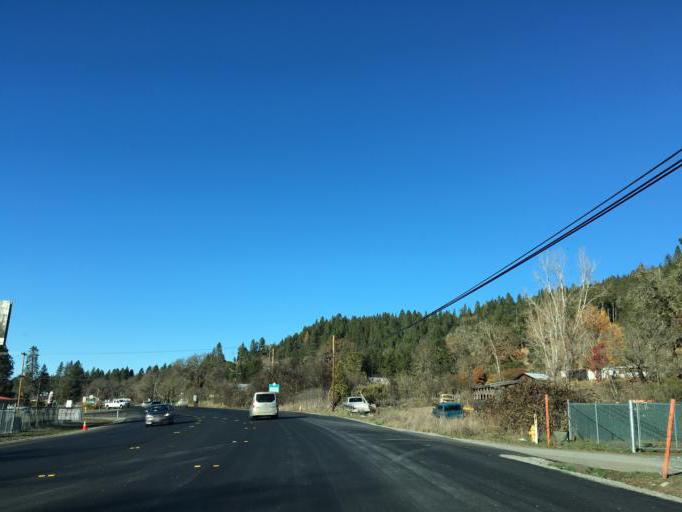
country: US
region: California
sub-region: Mendocino County
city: Laytonville
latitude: 39.6803
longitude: -123.4760
